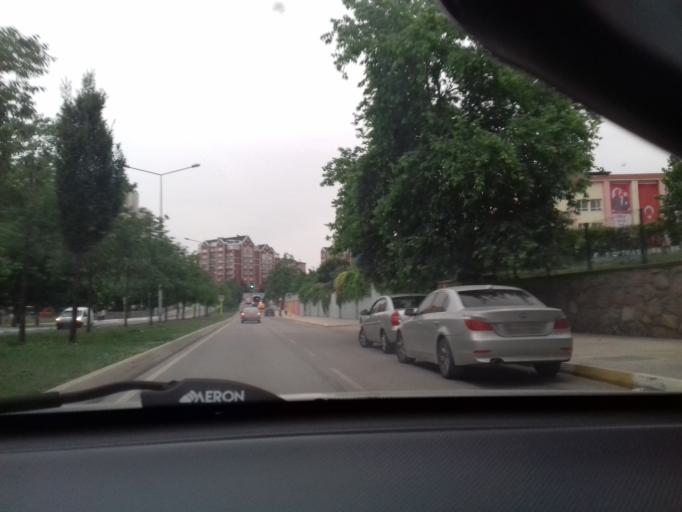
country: TR
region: Istanbul
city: Sultanbeyli
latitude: 40.9301
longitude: 29.2972
